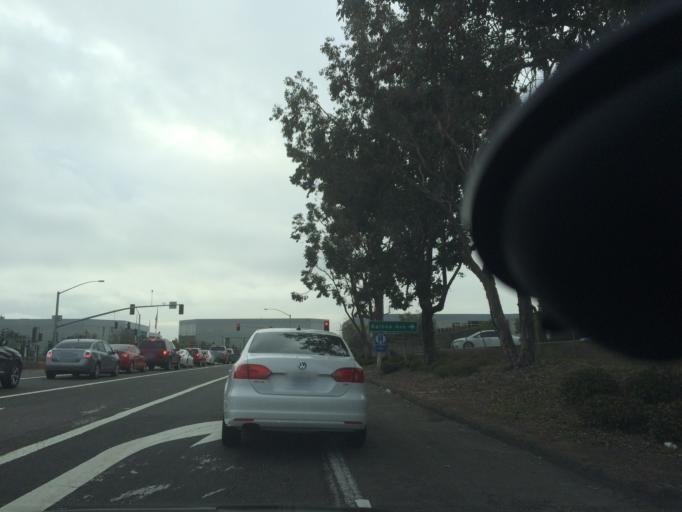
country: US
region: California
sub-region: San Diego County
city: San Diego
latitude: 32.8232
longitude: -117.1452
